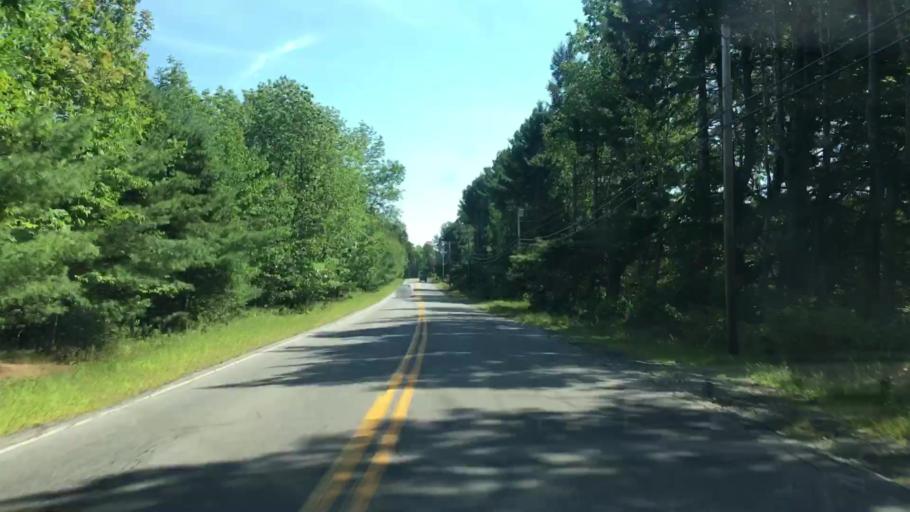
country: US
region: Maine
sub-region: Penobscot County
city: Bradford
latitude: 45.1737
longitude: -68.8523
